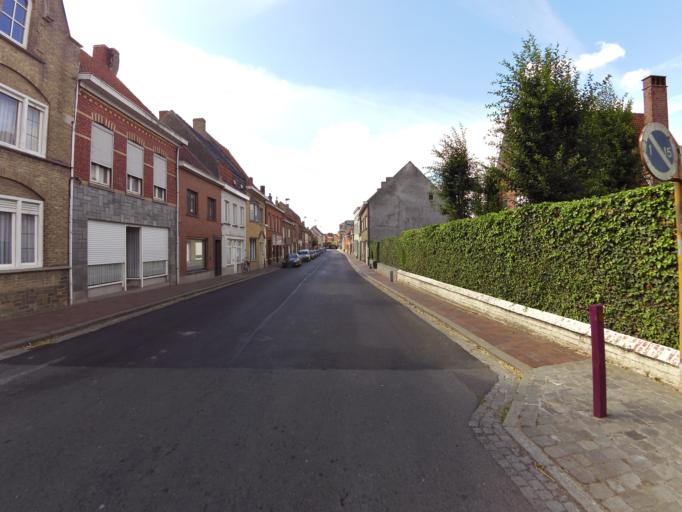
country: FR
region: Nord-Pas-de-Calais
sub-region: Departement du Nord
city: Hondschoote
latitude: 50.9204
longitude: 2.6225
